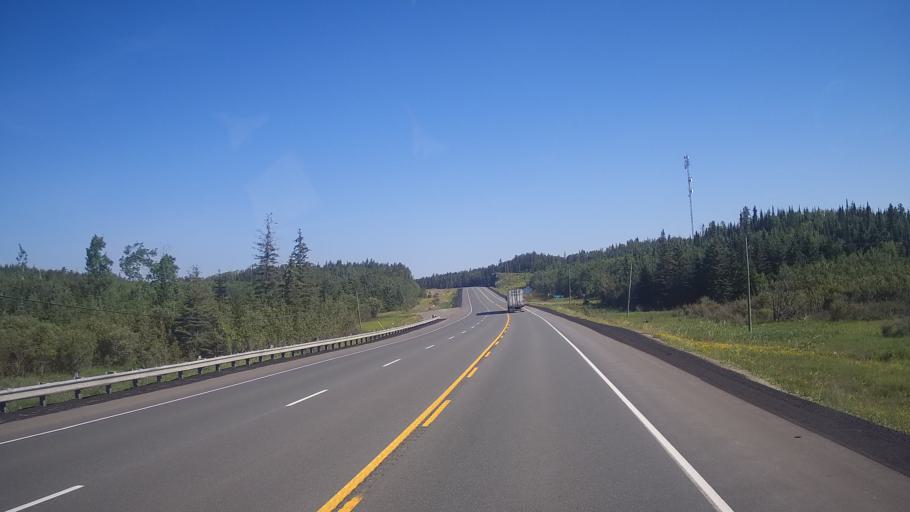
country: CA
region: Ontario
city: Dryden
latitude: 49.6351
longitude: -92.4403
